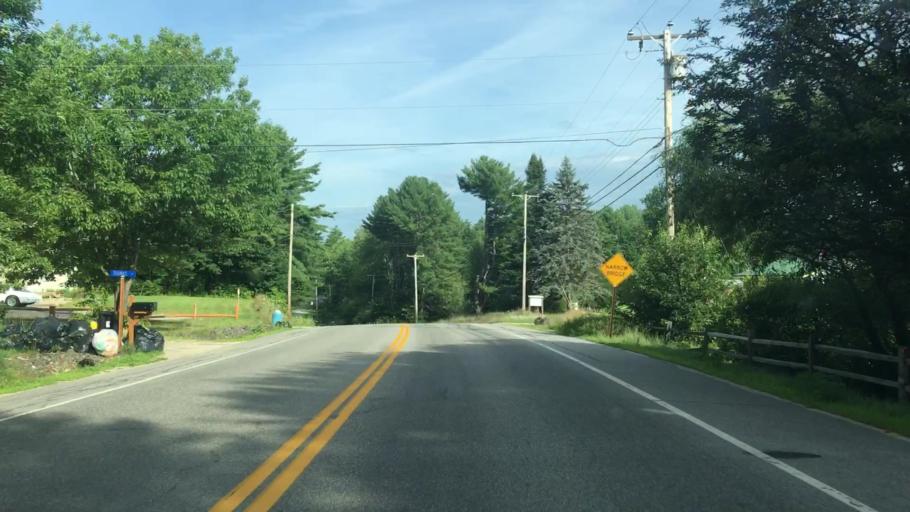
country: US
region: Maine
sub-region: York County
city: Limington
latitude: 43.7373
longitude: -70.6682
